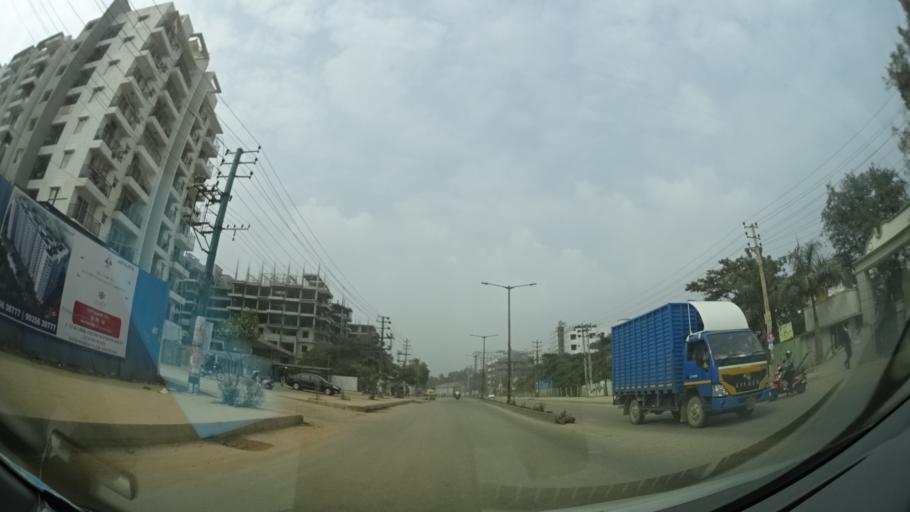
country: IN
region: Karnataka
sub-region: Bangalore Rural
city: Hoskote
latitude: 12.9828
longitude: 77.7559
